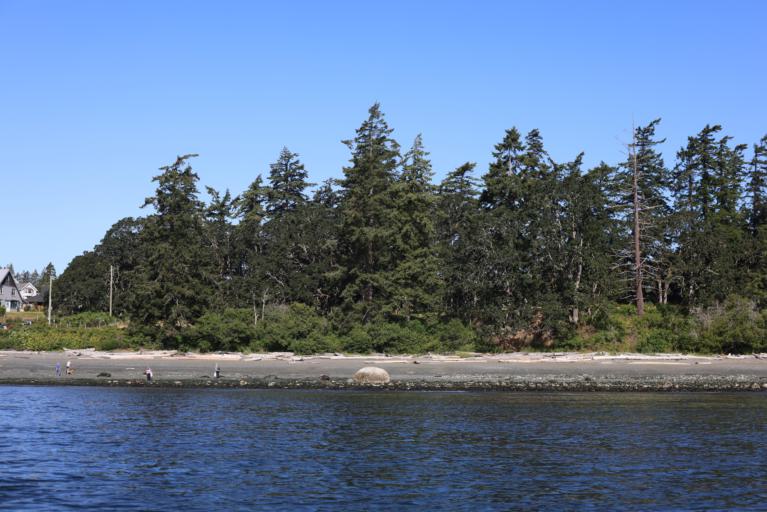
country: CA
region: British Columbia
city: Metchosin
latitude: 48.3665
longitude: -123.5298
